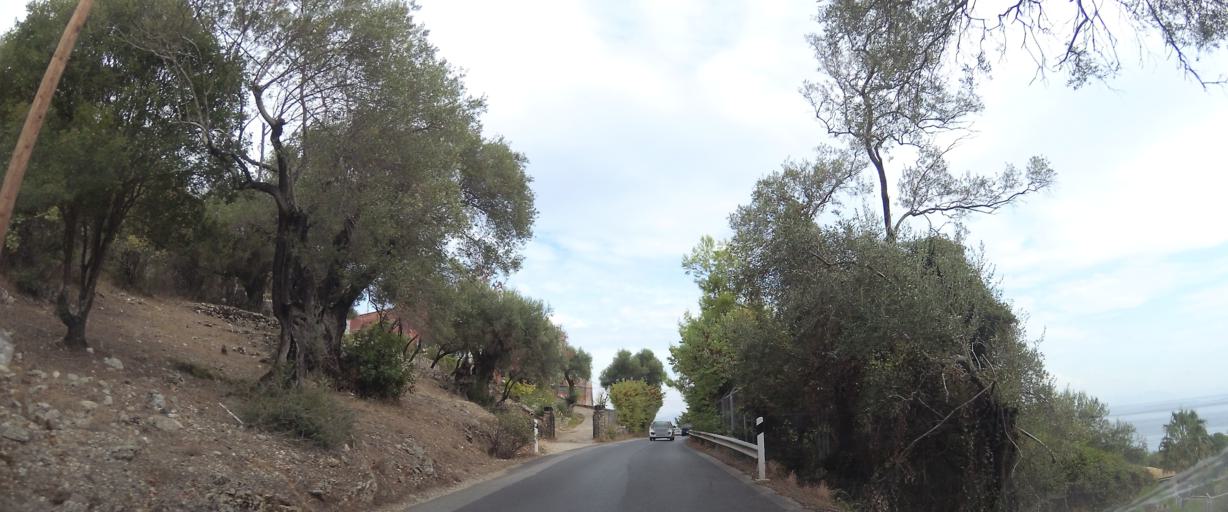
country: GR
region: Ionian Islands
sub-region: Nomos Kerkyras
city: Kontokali
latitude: 39.7146
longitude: 19.8627
